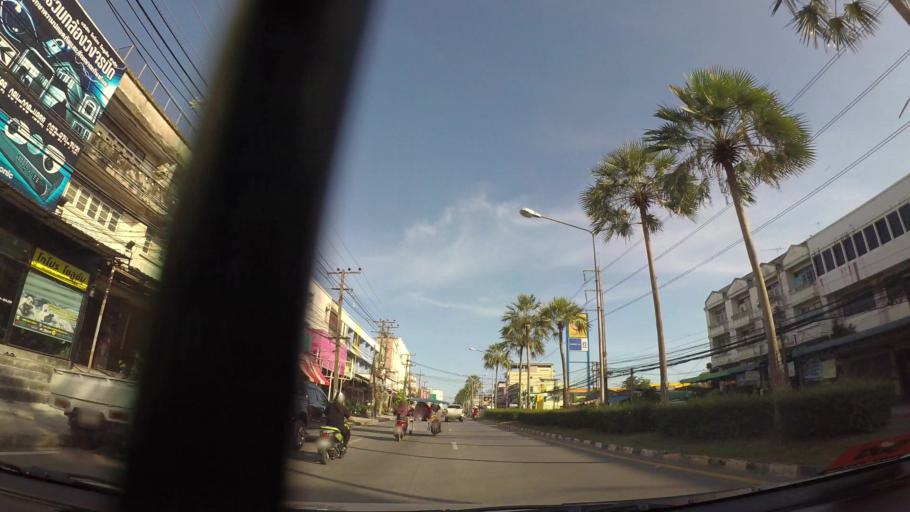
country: TH
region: Rayong
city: Rayong
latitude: 12.6918
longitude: 101.2736
